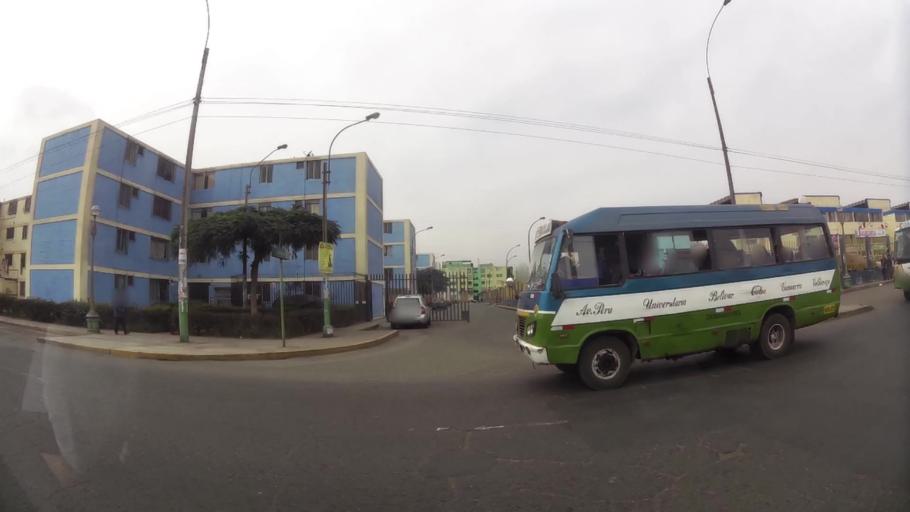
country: PE
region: Callao
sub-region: Callao
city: Callao
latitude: -12.0178
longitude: -77.1020
